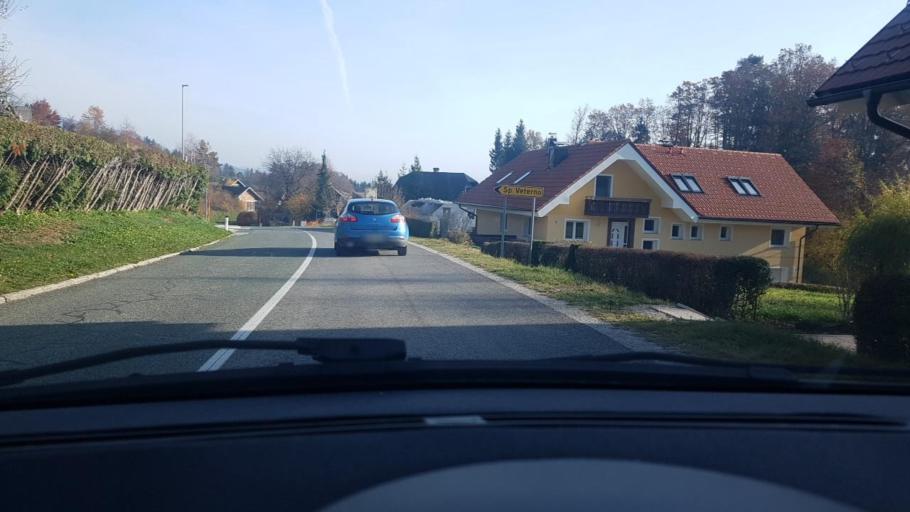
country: SI
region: Kranj
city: Golnik
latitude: 46.3326
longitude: 14.3155
